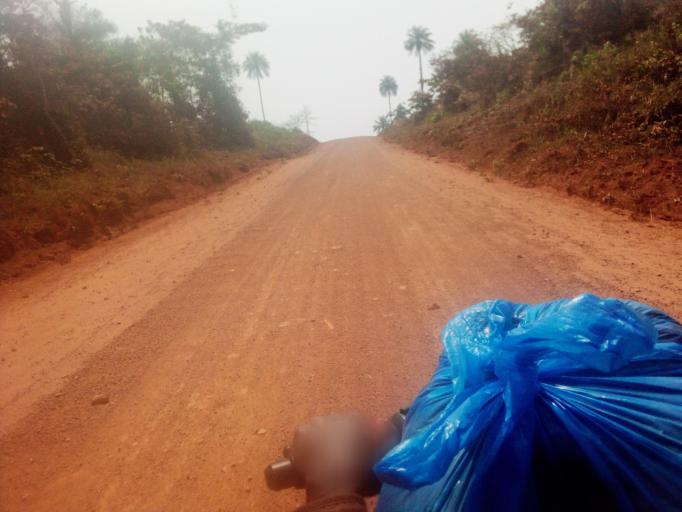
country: SL
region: Southern Province
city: Sumbuya
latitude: 7.6689
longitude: -11.9909
